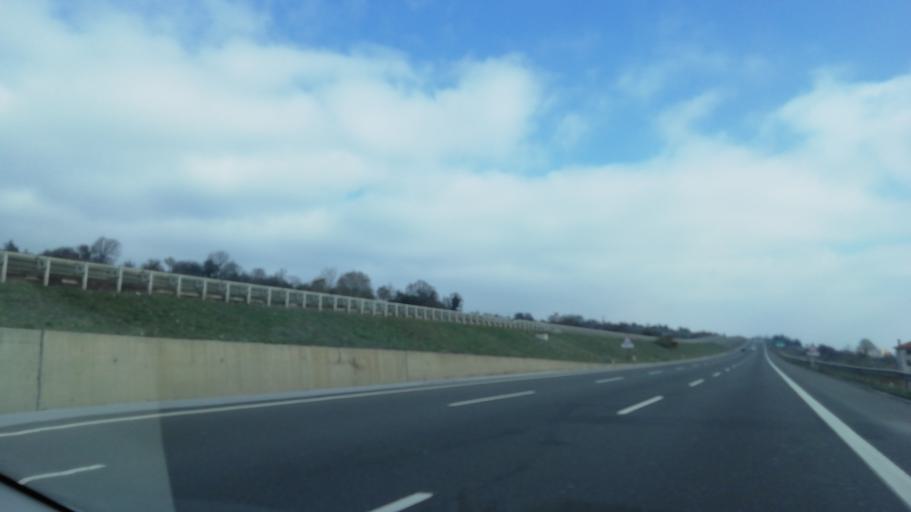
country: TR
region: Bolu
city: Bolu
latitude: 40.7223
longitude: 31.4963
